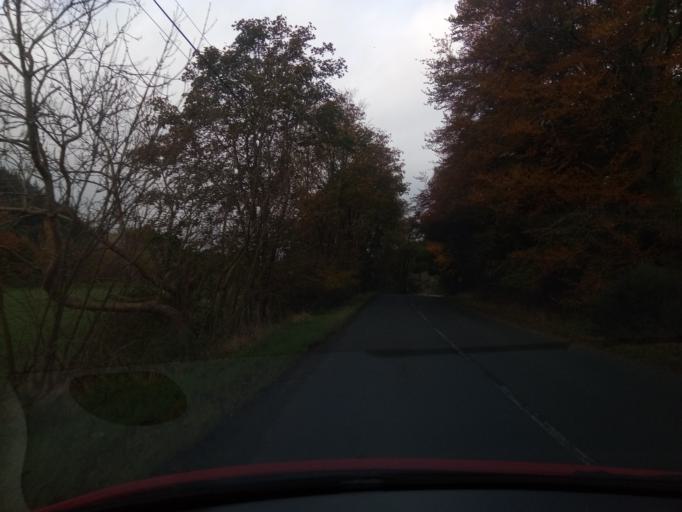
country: GB
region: Scotland
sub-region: The Scottish Borders
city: Selkirk
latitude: 55.6032
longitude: -2.8742
